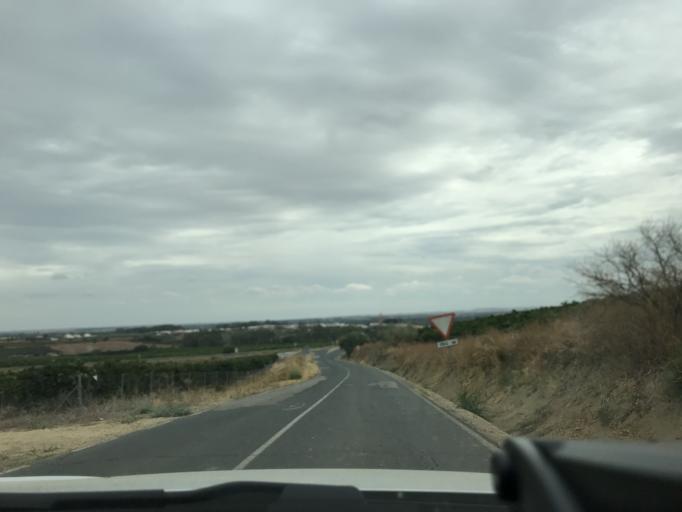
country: ES
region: Andalusia
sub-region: Provincia de Sevilla
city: Villanueva del Rio y Minas
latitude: 37.6382
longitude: -5.7017
